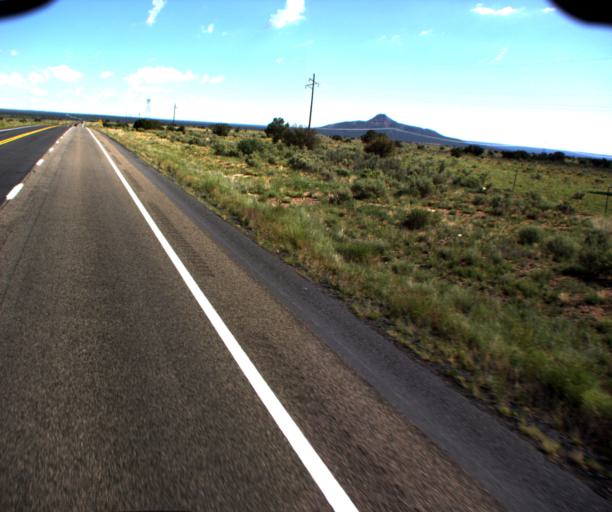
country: US
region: Arizona
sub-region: Coconino County
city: Grand Canyon Village
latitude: 35.7562
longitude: -112.1309
